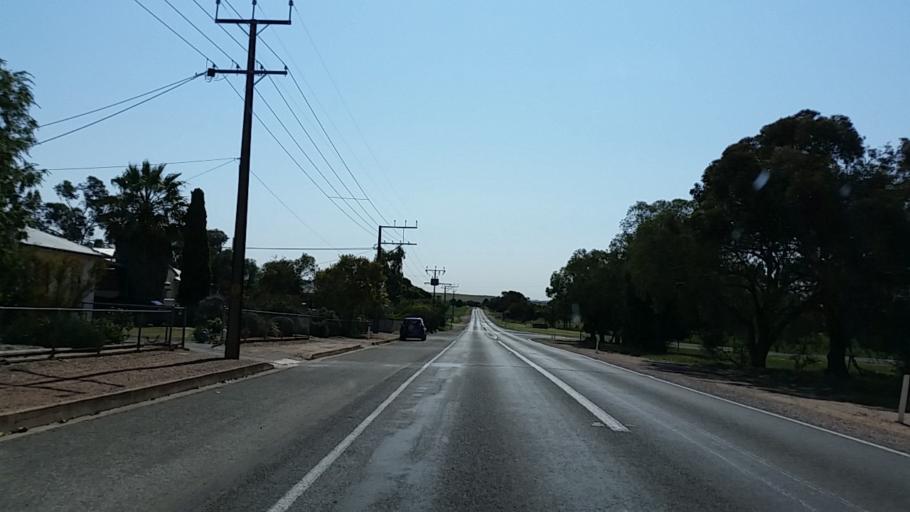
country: AU
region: South Australia
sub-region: Port Pirie City and Dists
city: Crystal Brook
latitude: -33.2592
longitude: 138.3567
